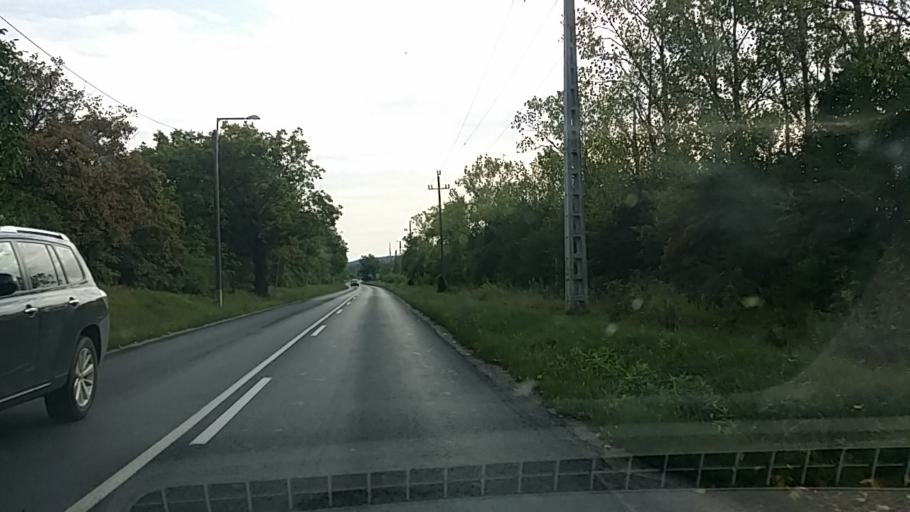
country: HU
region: Gyor-Moson-Sopron
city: Fertorakos
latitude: 47.7186
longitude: 16.6167
